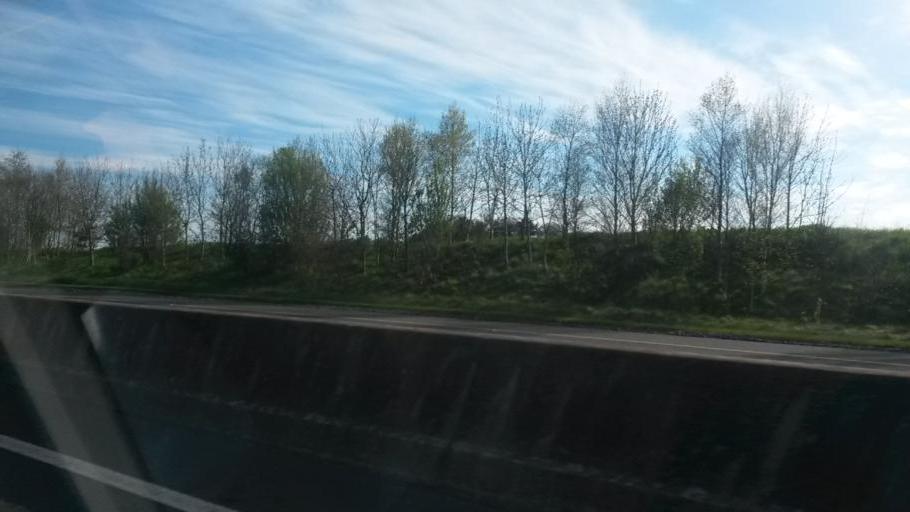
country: IE
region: Leinster
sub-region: An Mhi
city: Dunshaughlin
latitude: 53.5474
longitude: -6.5548
